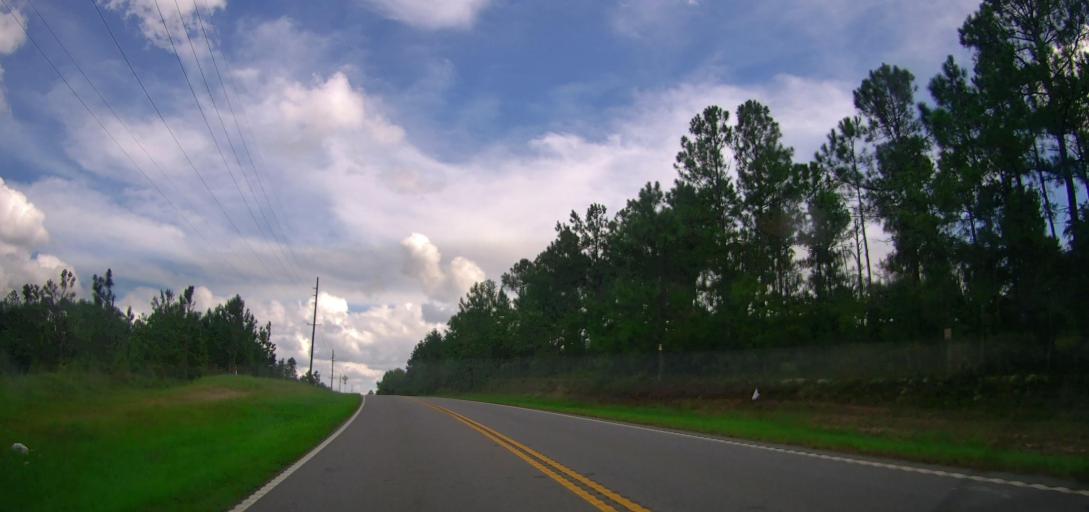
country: US
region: Georgia
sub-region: Talbot County
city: Talbotton
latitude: 32.6114
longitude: -84.4836
